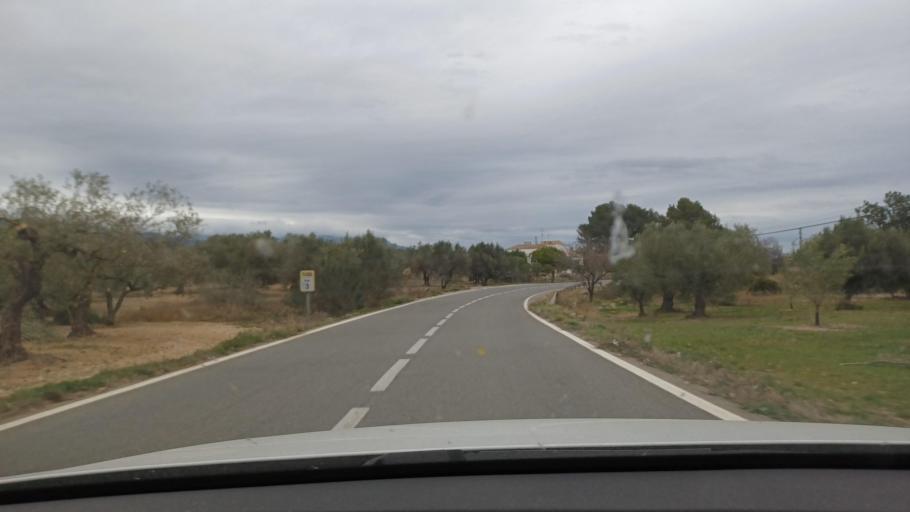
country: ES
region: Catalonia
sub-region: Provincia de Tarragona
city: Ulldecona
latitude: 40.6193
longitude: 0.3589
